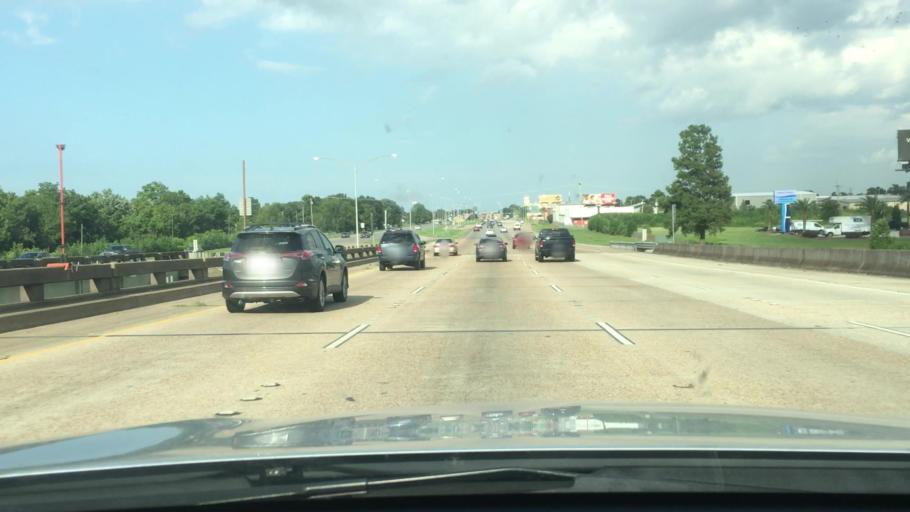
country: US
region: Louisiana
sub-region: Jefferson Parish
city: Kenner
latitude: 30.0066
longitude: -90.2777
